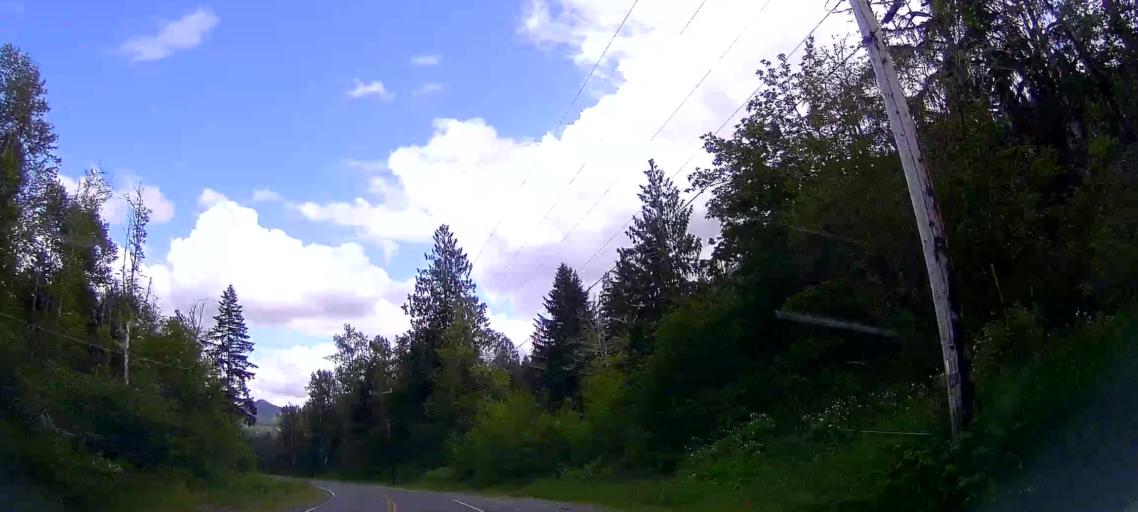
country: US
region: Washington
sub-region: Skagit County
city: Sedro-Woolley
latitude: 48.6729
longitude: -122.1525
